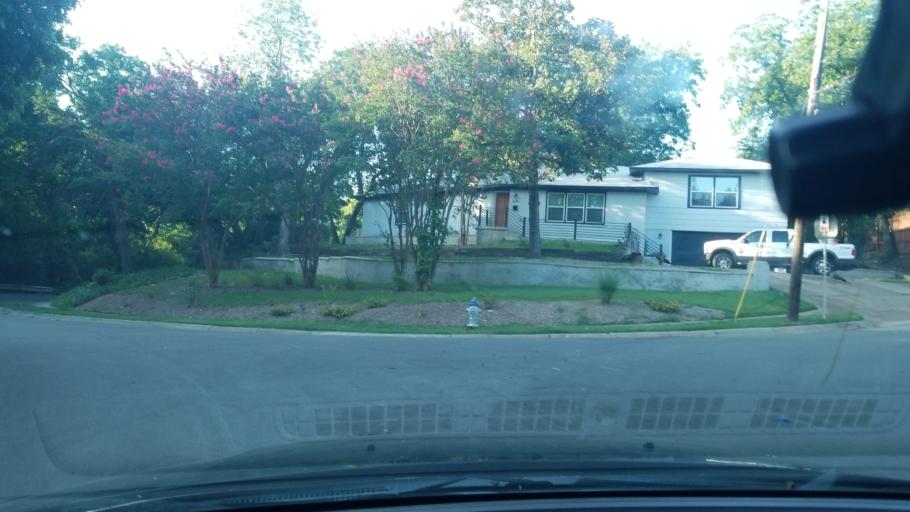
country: US
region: Texas
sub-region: Dallas County
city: Dallas
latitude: 32.7291
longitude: -96.8206
